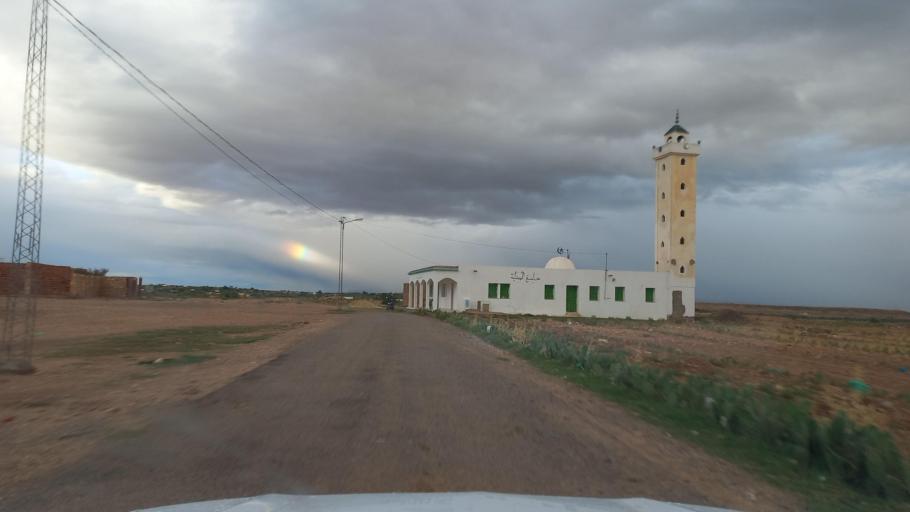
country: TN
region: Al Qasrayn
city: Kasserine
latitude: 35.2647
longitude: 8.9347
